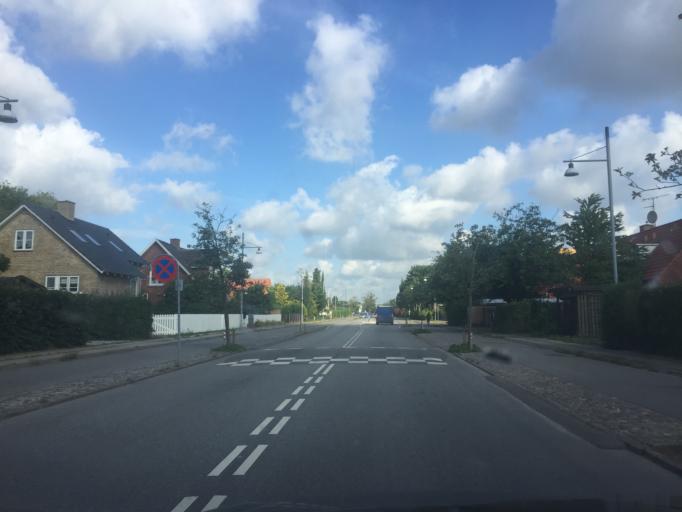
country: DK
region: Capital Region
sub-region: Glostrup Kommune
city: Glostrup
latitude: 55.6730
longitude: 12.3996
